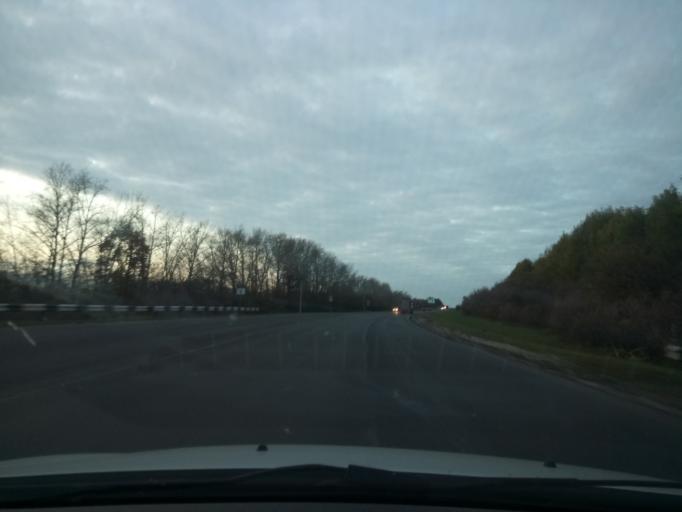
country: RU
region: Nizjnij Novgorod
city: Bol'shoye Murashkino
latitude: 55.8028
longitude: 44.7642
